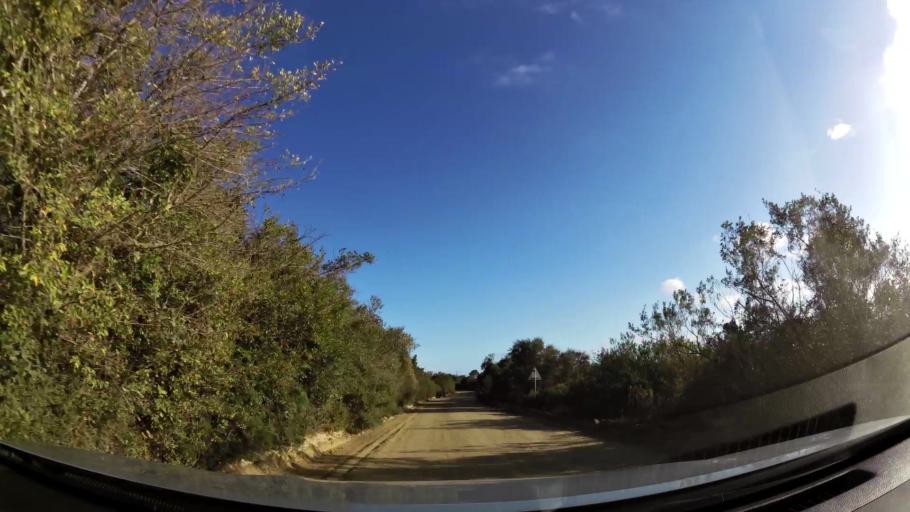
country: ZA
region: Western Cape
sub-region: Eden District Municipality
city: George
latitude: -33.9907
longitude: 22.5634
